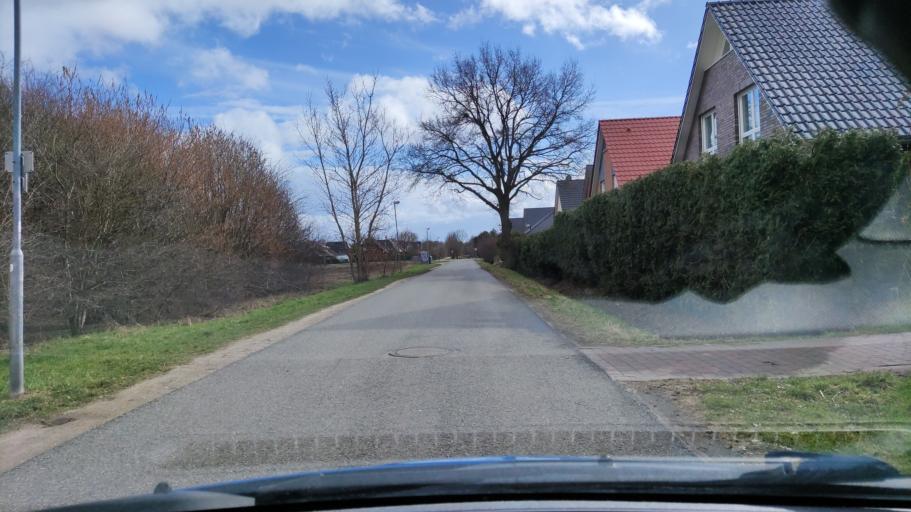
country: DE
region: Lower Saxony
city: Winsen
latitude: 53.3618
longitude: 10.2236
